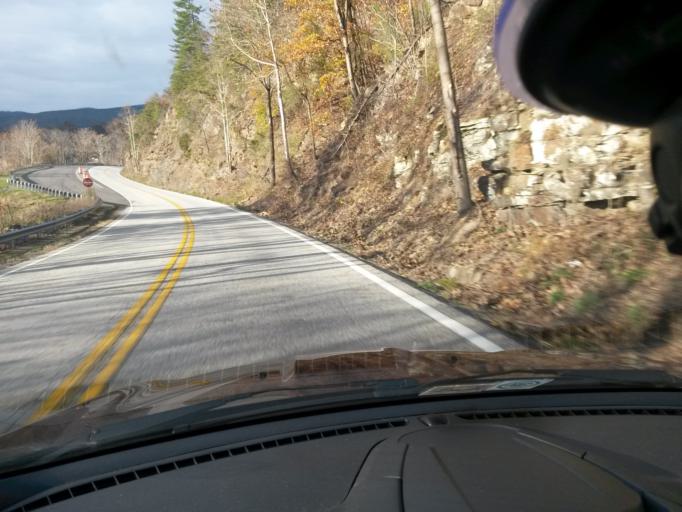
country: US
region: Virginia
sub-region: Rockbridge County
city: Glasgow
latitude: 37.5914
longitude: -79.3793
